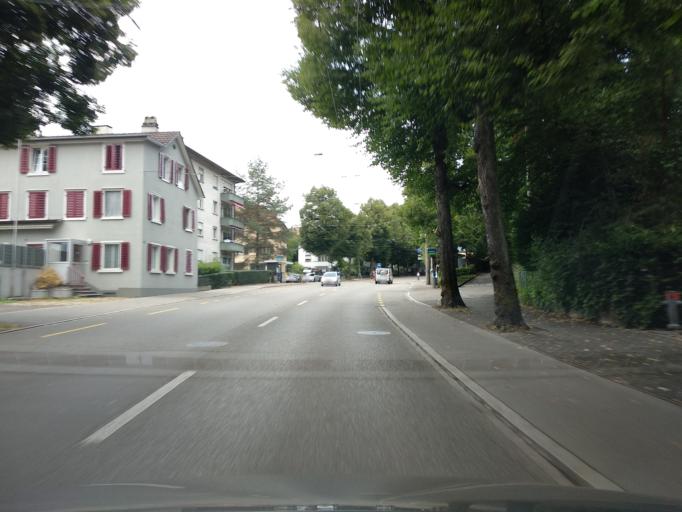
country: CH
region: Zurich
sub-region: Bezirk Winterthur
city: Veltheim
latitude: 47.5109
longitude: 8.7218
